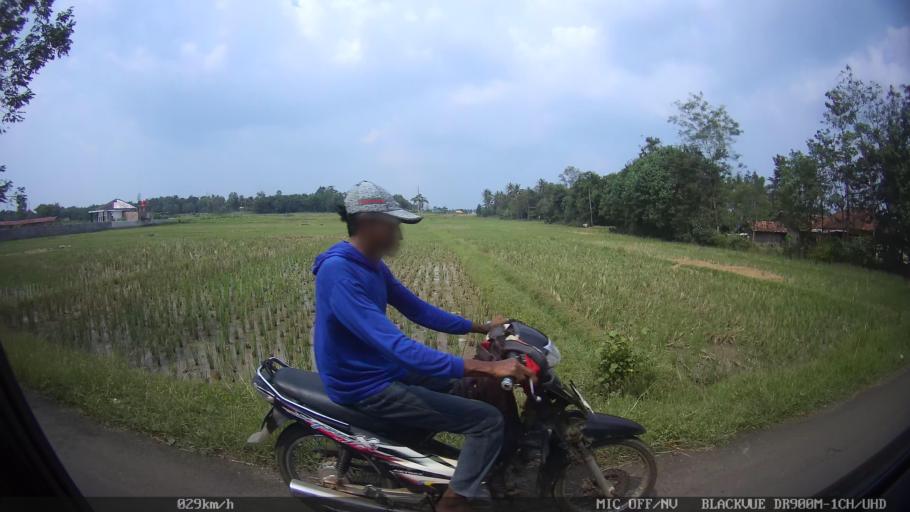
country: ID
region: Lampung
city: Gadingrejo
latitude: -5.3573
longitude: 105.0394
